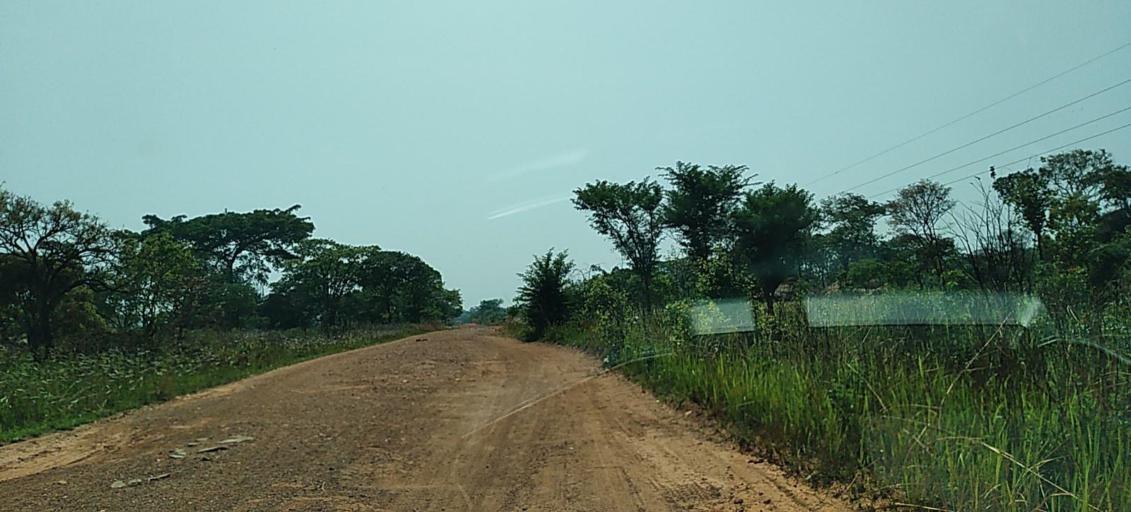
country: ZM
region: North-Western
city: Kansanshi
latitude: -12.0068
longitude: 26.5256
